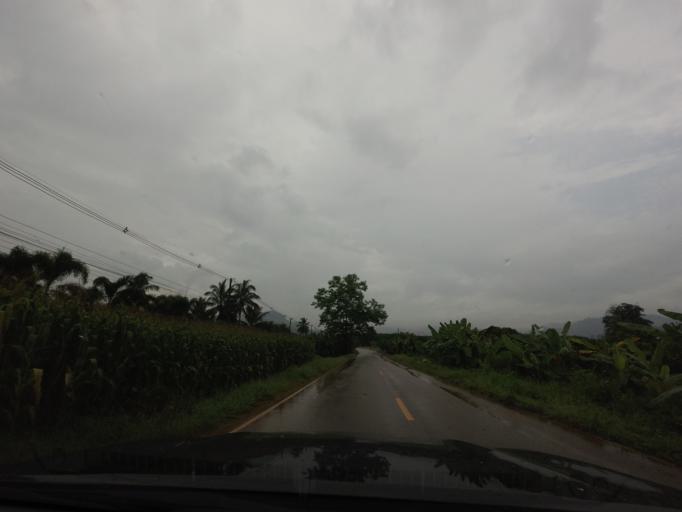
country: TH
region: Loei
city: Pak Chom
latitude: 18.2038
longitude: 102.0662
